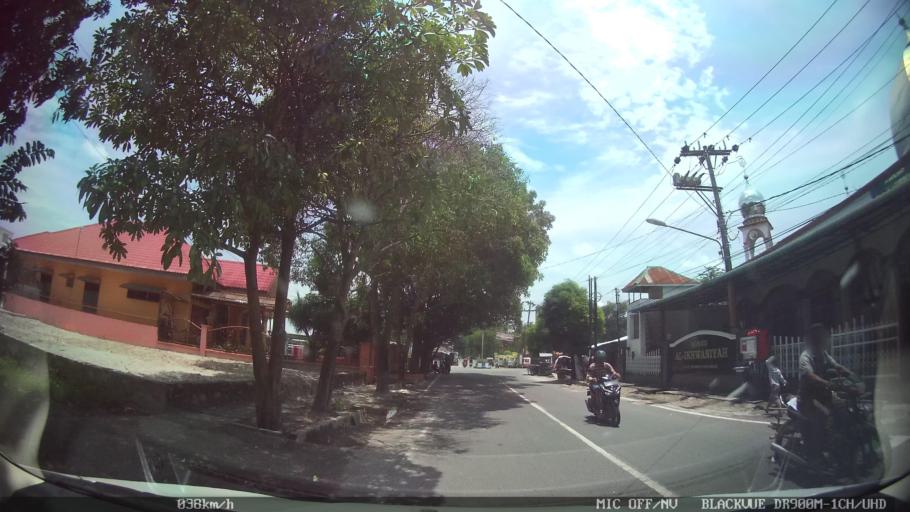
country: ID
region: North Sumatra
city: Percut
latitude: 3.5541
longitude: 98.8701
